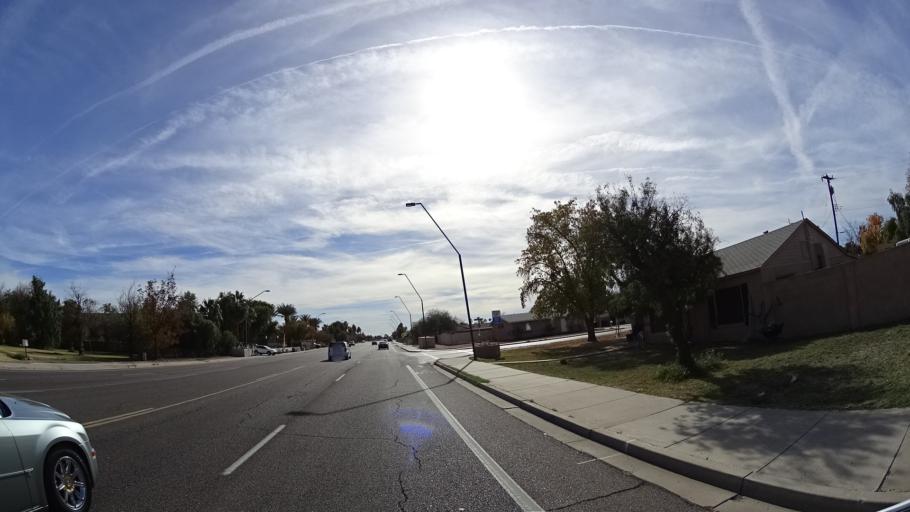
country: US
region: Arizona
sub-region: Maricopa County
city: Gilbert
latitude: 33.3450
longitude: -111.7898
